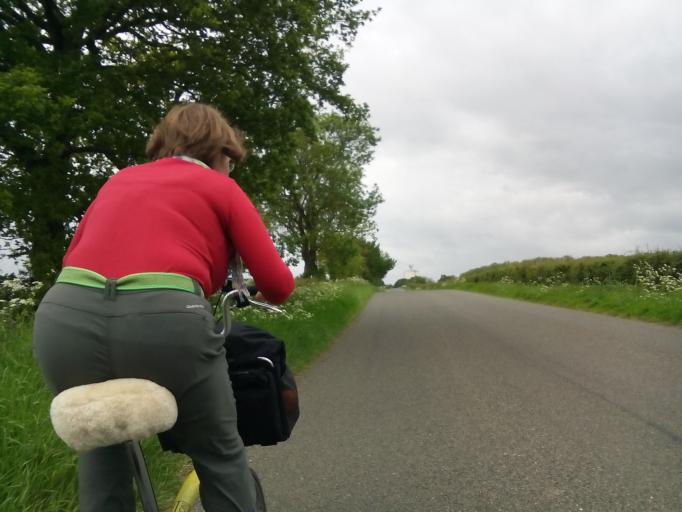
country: GB
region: England
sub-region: Northamptonshire
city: Oundle
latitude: 52.5065
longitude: -0.4901
